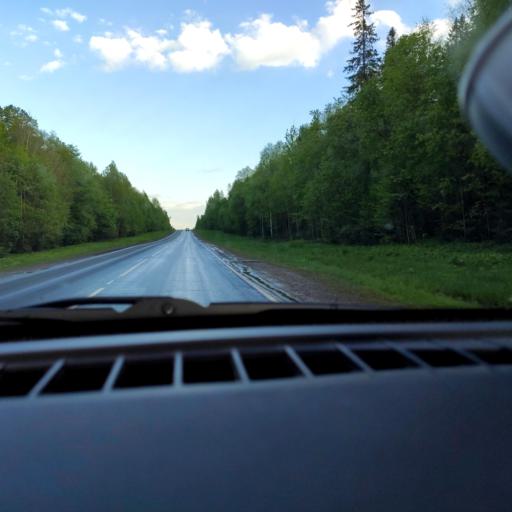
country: RU
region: Perm
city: Perm
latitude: 58.1830
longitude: 56.2226
